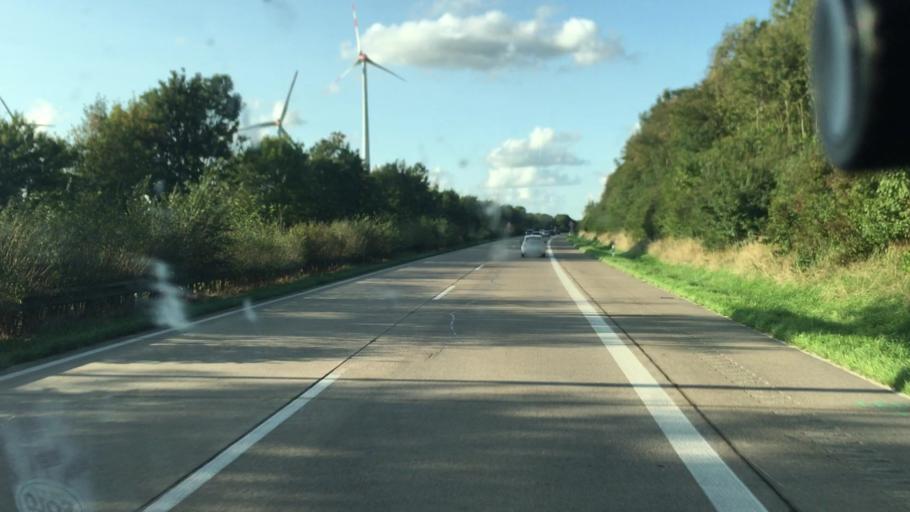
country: DE
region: Lower Saxony
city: Sande
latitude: 53.4995
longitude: 7.9967
